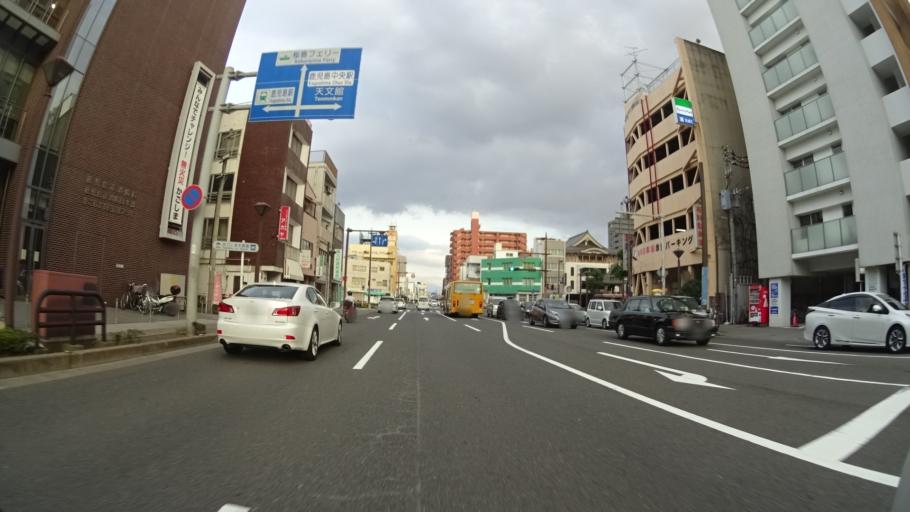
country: JP
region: Kagoshima
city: Kagoshima-shi
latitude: 31.5981
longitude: 130.5579
